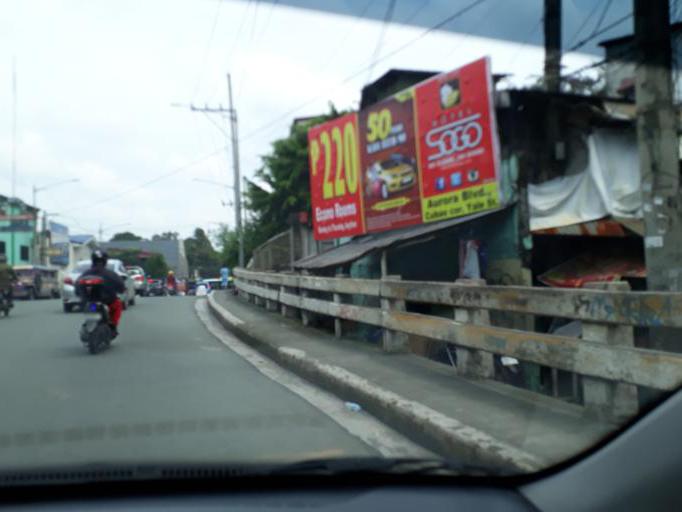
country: PH
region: Metro Manila
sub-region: Quezon City
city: Quezon City
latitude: 14.6297
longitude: 121.0557
